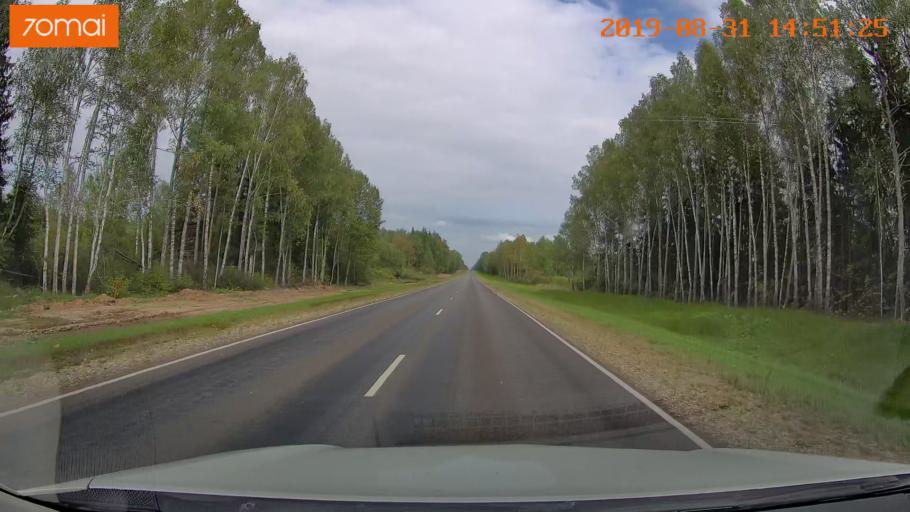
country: RU
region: Kaluga
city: Spas-Demensk
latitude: 54.2685
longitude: 33.8140
